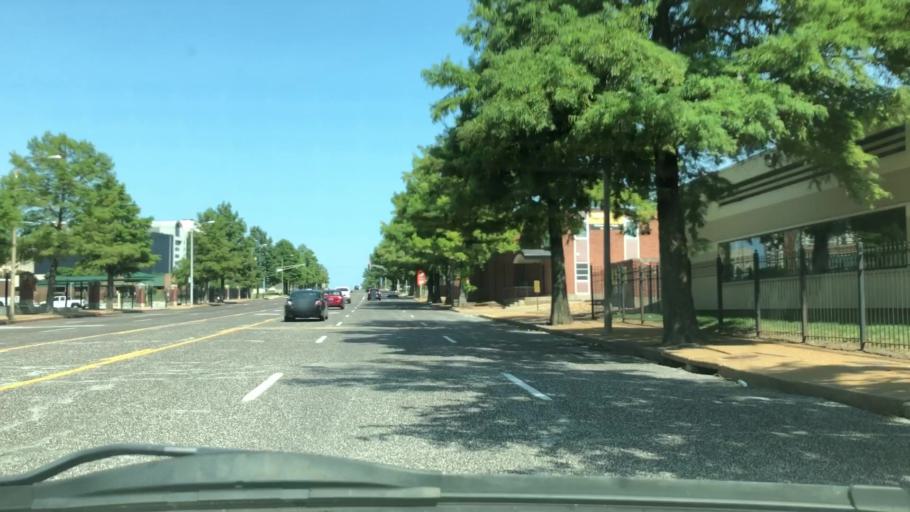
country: US
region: Missouri
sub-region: City of Saint Louis
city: St. Louis
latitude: 38.6309
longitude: -90.2252
